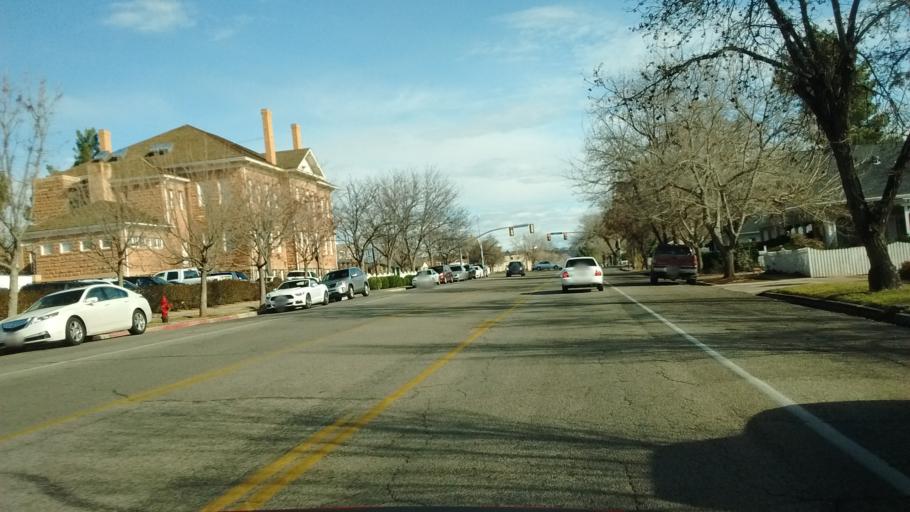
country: US
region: Utah
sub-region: Washington County
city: Saint George
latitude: 37.1065
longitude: -113.5847
